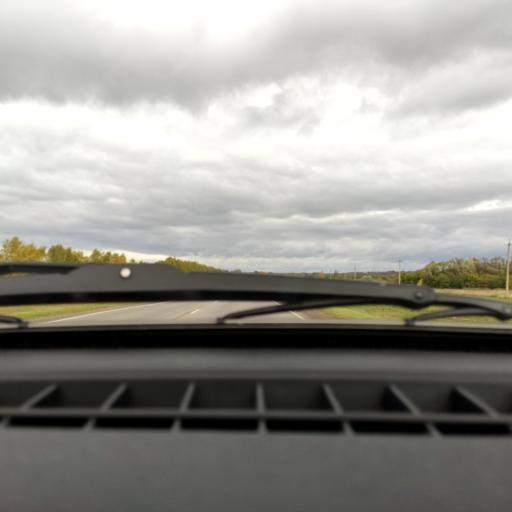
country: RU
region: Bashkortostan
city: Rayevskiy
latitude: 54.0225
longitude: 54.8873
